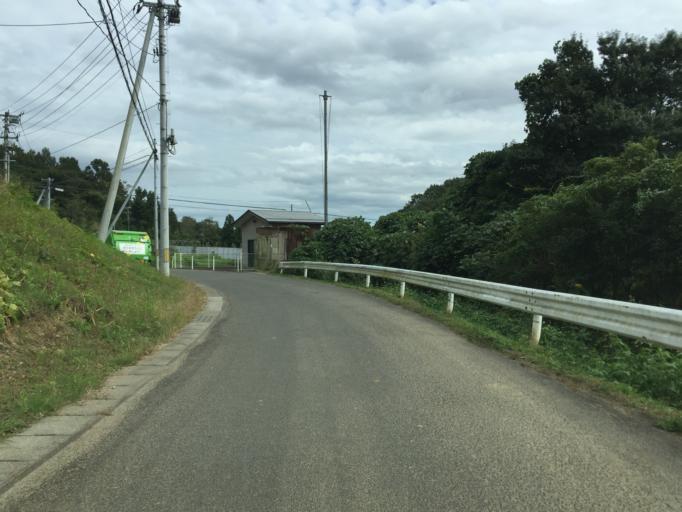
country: JP
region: Fukushima
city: Fukushima-shi
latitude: 37.6884
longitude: 140.4592
